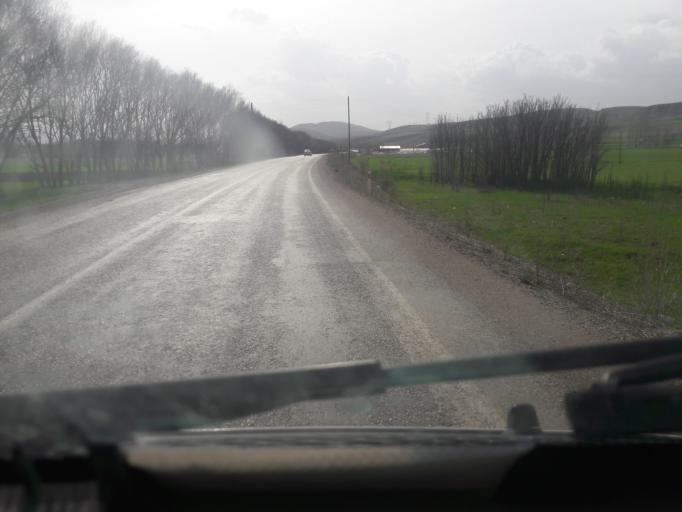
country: TR
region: Gumushane
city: Kelkit
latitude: 40.1427
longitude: 39.4224
